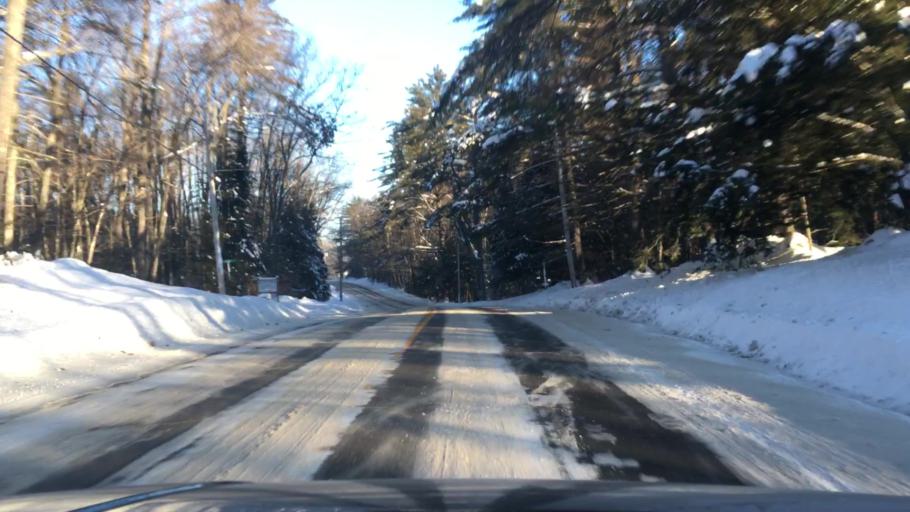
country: US
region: Maine
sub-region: Oxford County
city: Lovell
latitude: 44.1381
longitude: -70.9784
